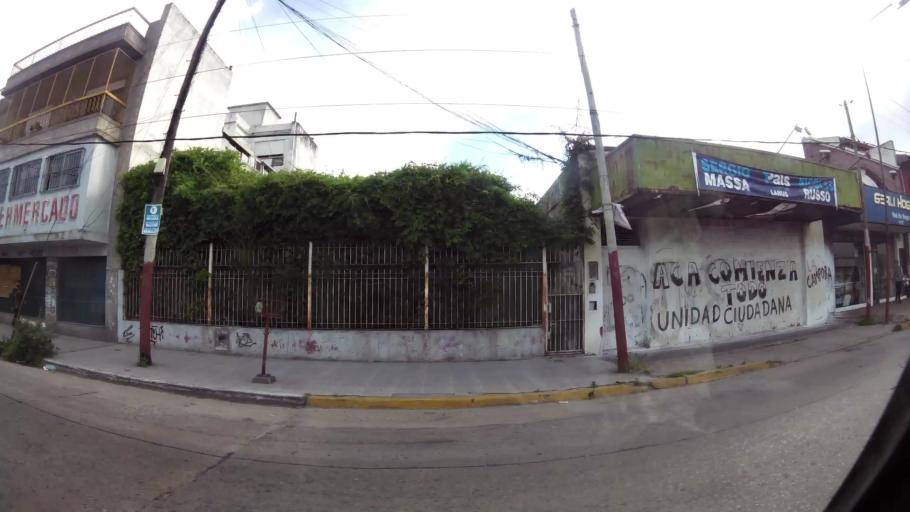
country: AR
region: Buenos Aires
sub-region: Partido de Lanus
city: Lanus
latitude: -34.6911
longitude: -58.3777
